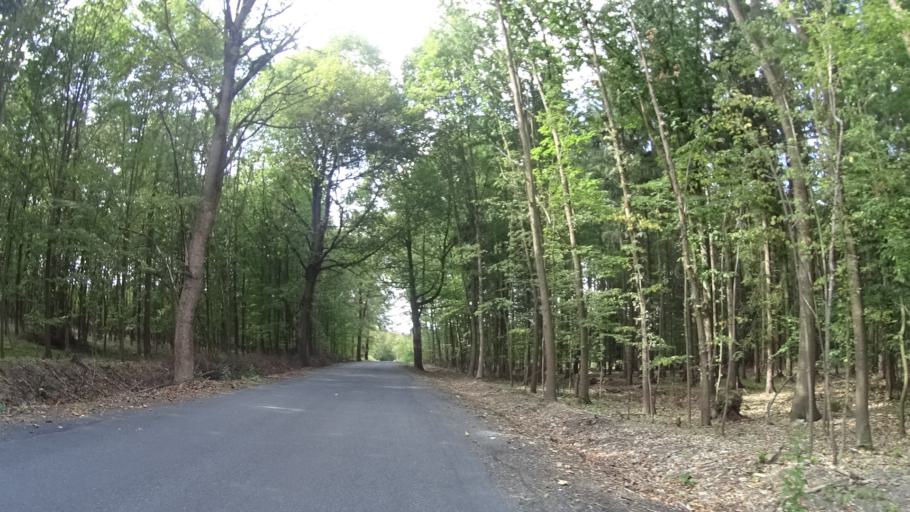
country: CZ
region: Olomoucky
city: Bila Lhota
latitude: 49.7311
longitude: 17.0092
